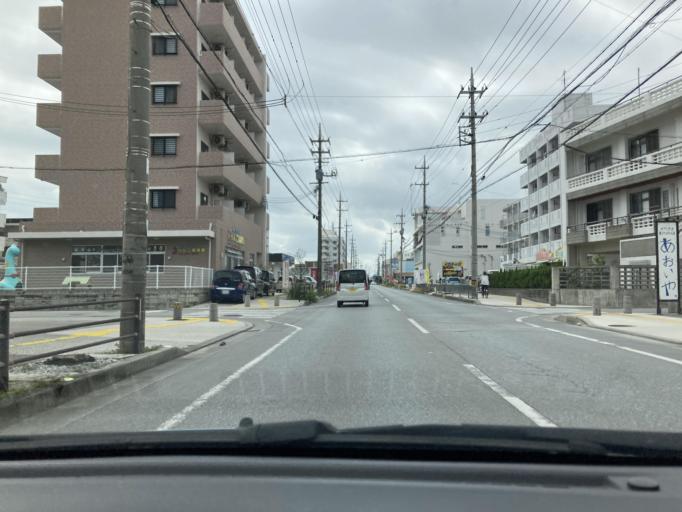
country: JP
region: Okinawa
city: Ginowan
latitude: 26.2460
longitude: 127.7698
